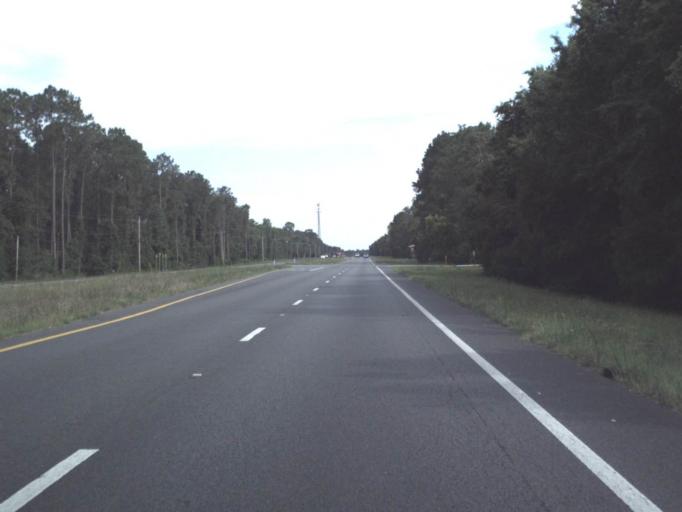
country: US
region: Florida
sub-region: Clay County
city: Green Cove Springs
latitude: 29.8979
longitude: -81.6725
